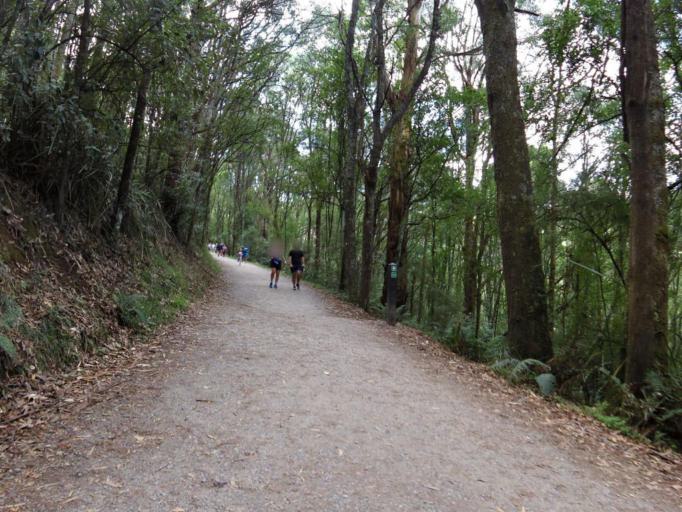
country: AU
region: Victoria
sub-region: Yarra Ranges
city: Ferny Creek
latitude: -37.8793
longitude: 145.3161
